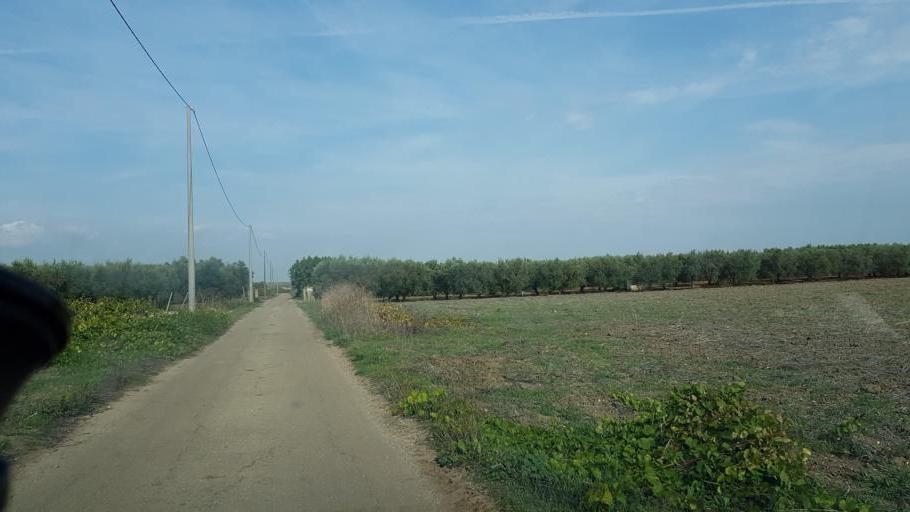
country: IT
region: Apulia
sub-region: Provincia di Brindisi
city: San Pancrazio Salentino
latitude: 40.4287
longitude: 17.8590
